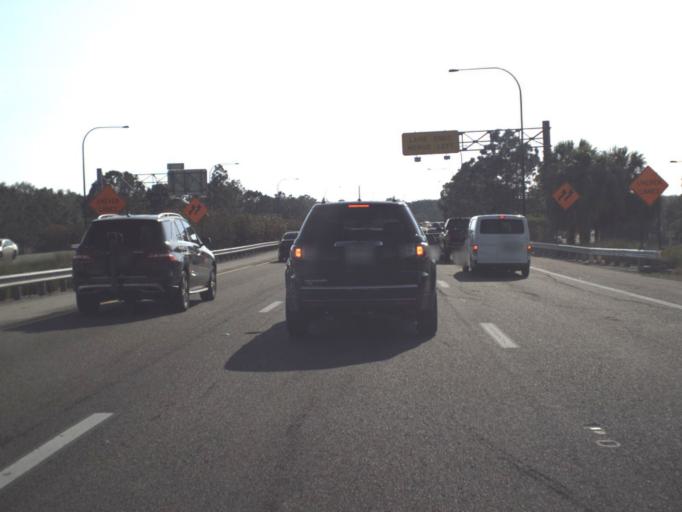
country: US
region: Florida
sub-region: Orange County
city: Orlovista
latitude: 28.5489
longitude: -81.4710
